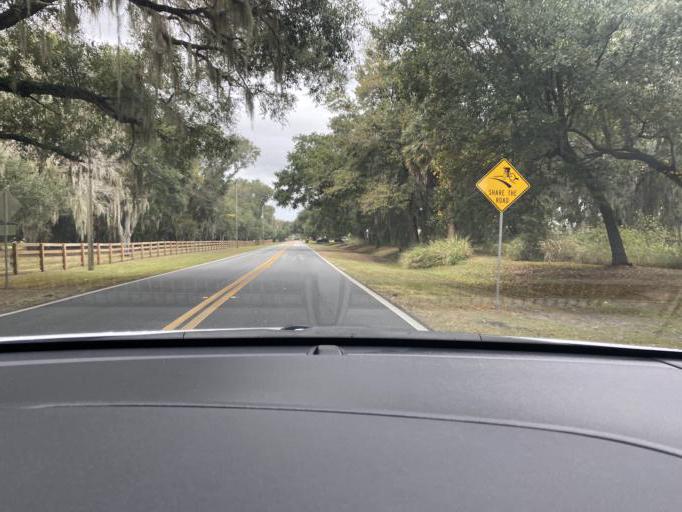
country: US
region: Florida
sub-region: Lake County
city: Clermont
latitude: 28.5717
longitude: -81.7807
